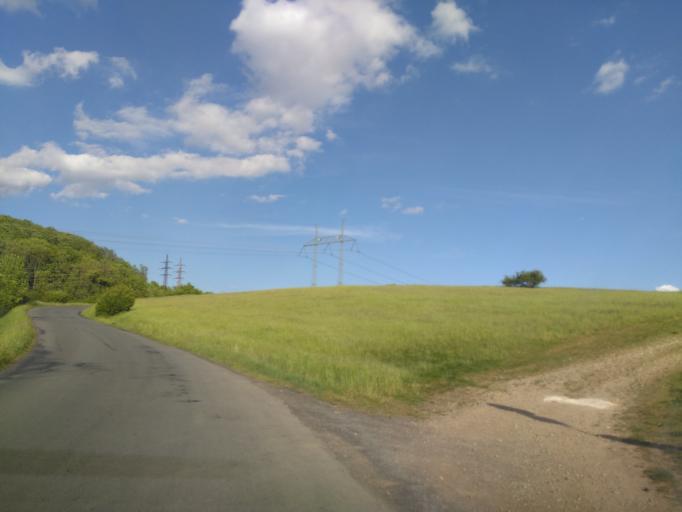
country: CZ
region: Central Bohemia
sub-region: Okres Beroun
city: Beroun
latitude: 49.9258
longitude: 14.0854
